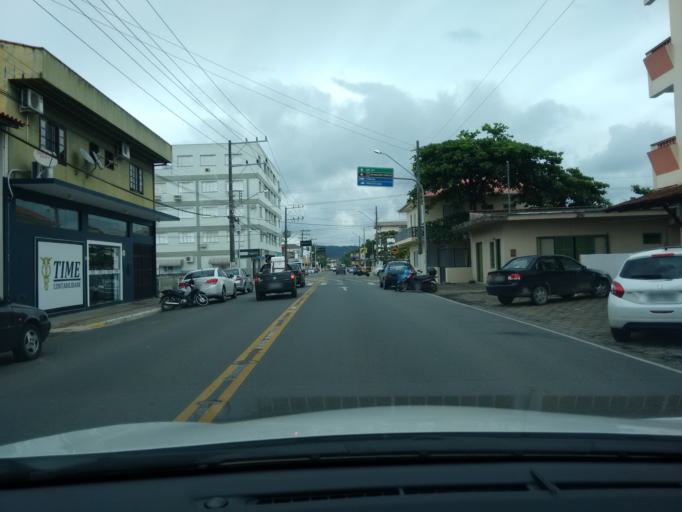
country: BR
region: Santa Catarina
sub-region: Penha
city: Penha
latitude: -26.7582
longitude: -48.6760
